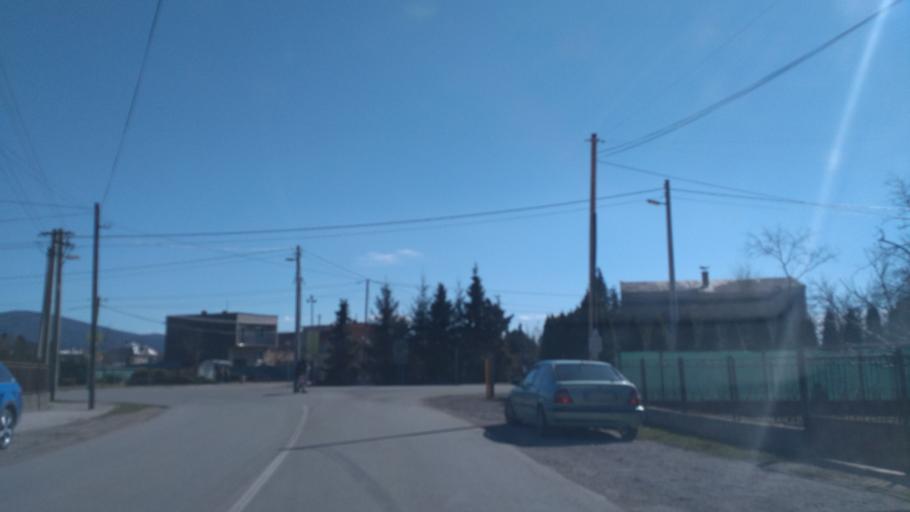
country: SK
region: Kosicky
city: Kosice
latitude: 48.6074
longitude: 21.3223
